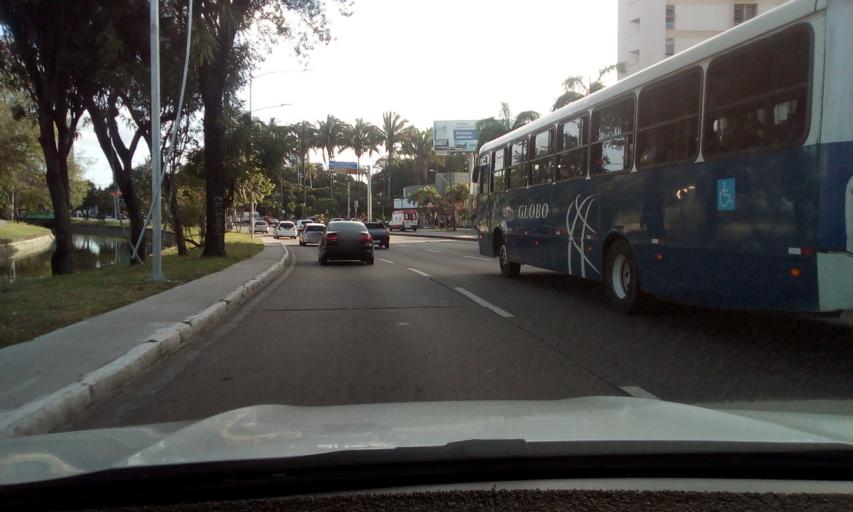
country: BR
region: Pernambuco
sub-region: Recife
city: Recife
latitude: -8.0548
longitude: -34.8976
